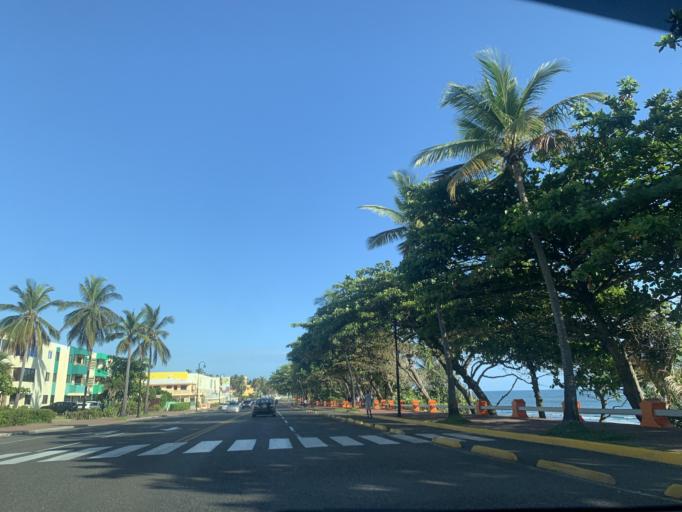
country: DO
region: Puerto Plata
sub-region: Puerto Plata
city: Puerto Plata
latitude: 19.7949
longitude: -70.6826
